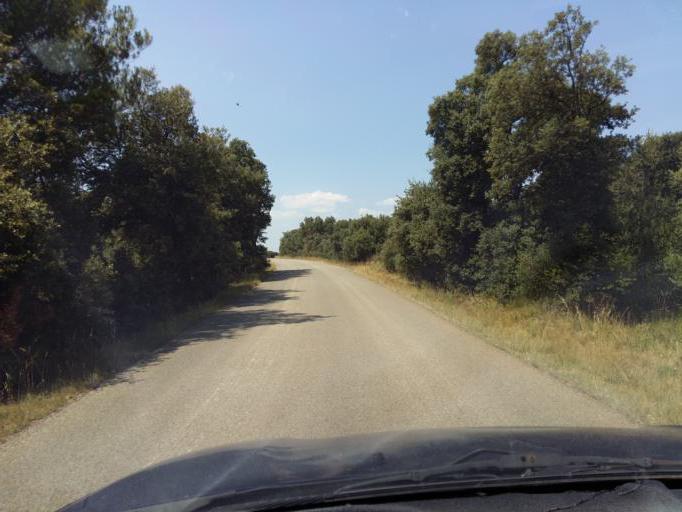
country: FR
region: Provence-Alpes-Cote d'Azur
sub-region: Departement du Vaucluse
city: Camaret-sur-Aigues
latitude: 44.1919
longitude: 4.8775
